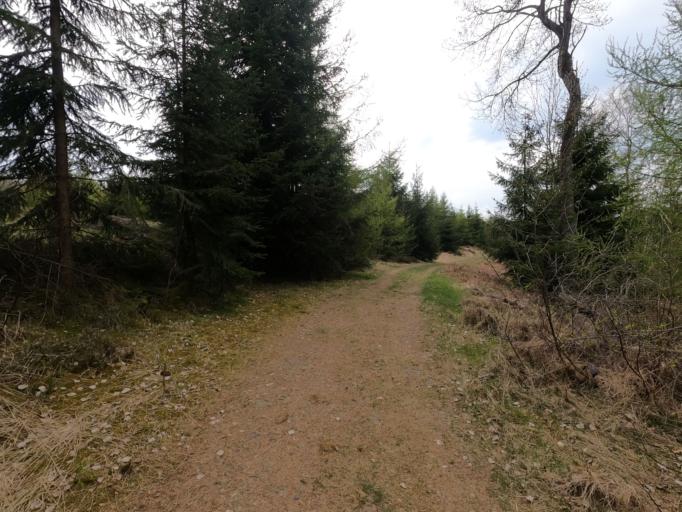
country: DE
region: North Rhine-Westphalia
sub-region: Regierungsbezirk Arnsberg
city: Herscheid
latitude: 51.1622
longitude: 7.7322
